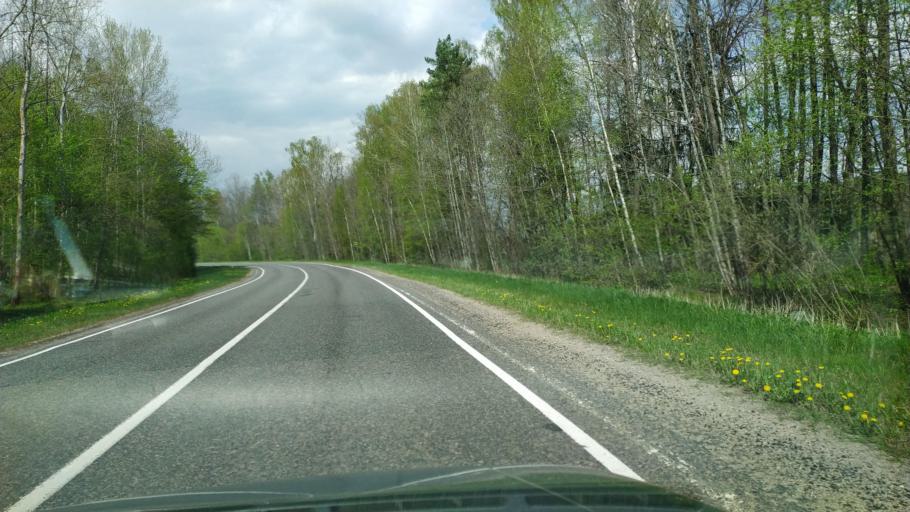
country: BY
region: Brest
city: Pruzhany
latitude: 52.3765
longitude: 24.5888
